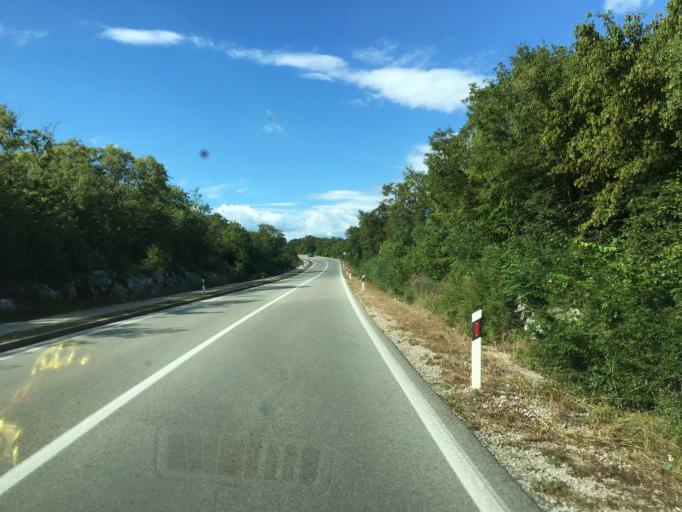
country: HR
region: Primorsko-Goranska
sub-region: Grad Krk
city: Krk
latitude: 45.0817
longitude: 14.5438
